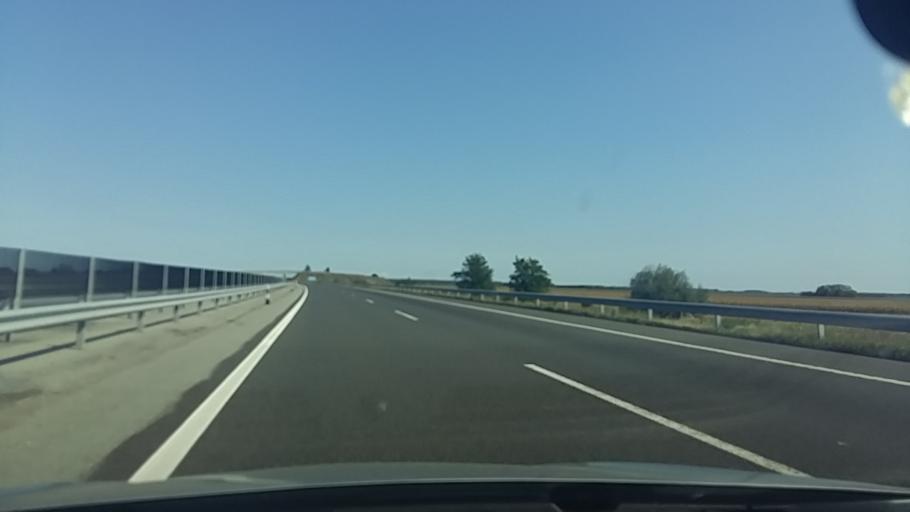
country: HU
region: Hajdu-Bihar
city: Gorbehaza
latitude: 47.7957
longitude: 21.2788
